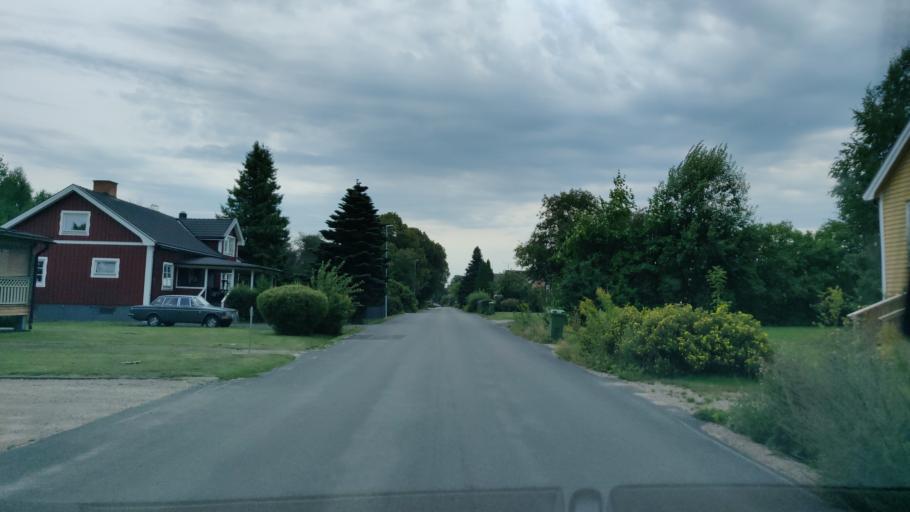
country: SE
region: Vaermland
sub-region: Munkfors Kommun
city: Munkfors
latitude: 59.8356
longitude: 13.5206
